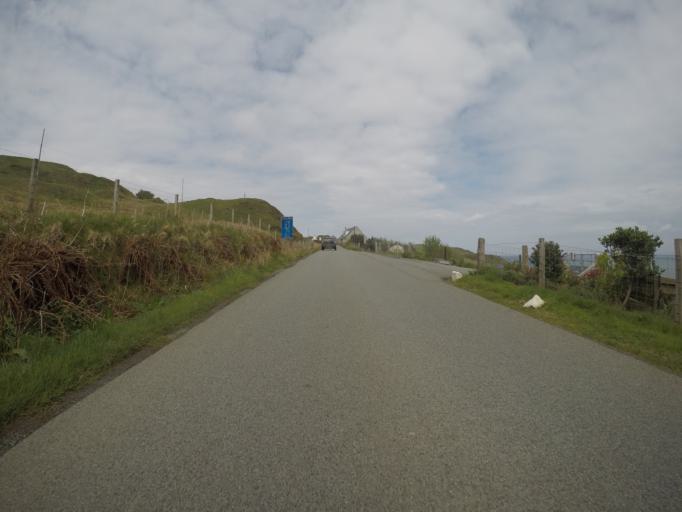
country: GB
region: Scotland
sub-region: Highland
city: Portree
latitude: 57.6360
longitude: -6.2405
